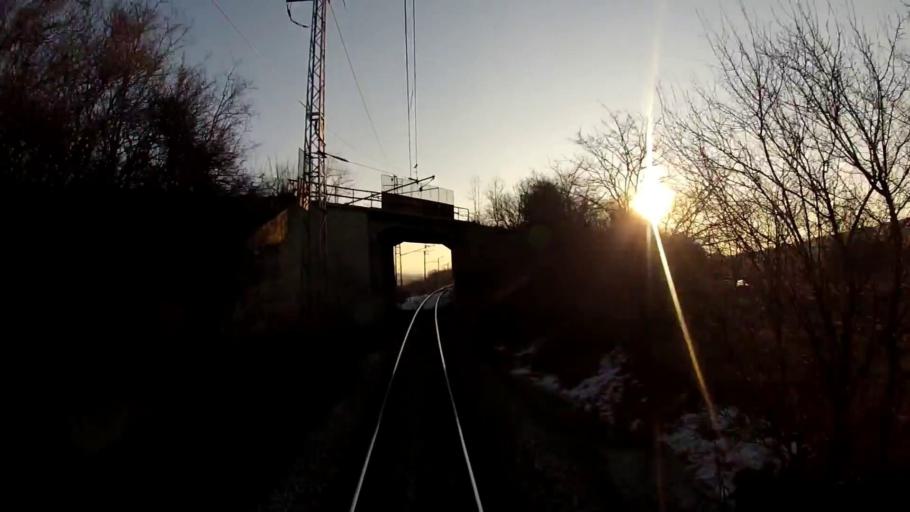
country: BG
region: Sofiya
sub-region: Obshtina Slivnitsa
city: Slivnitsa
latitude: 42.8768
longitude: 23.0168
